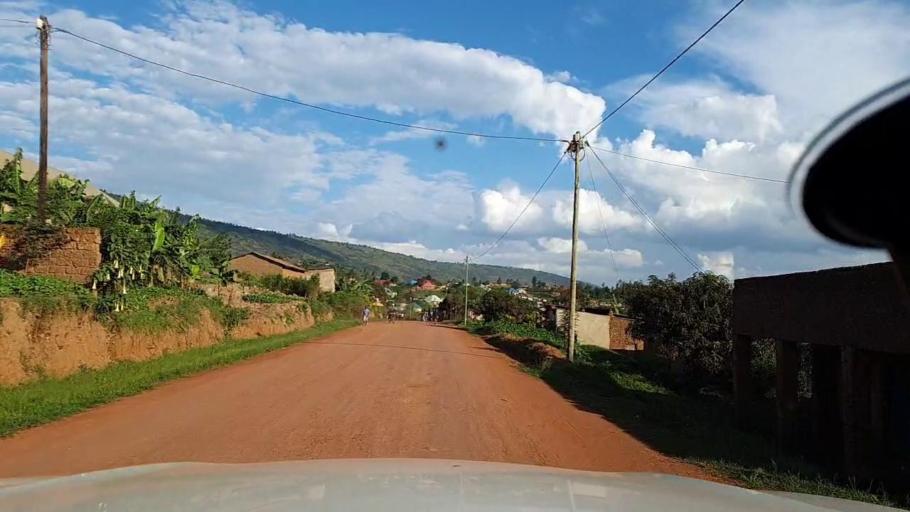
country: RW
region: Kigali
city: Kigali
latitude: -1.8935
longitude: 29.9608
